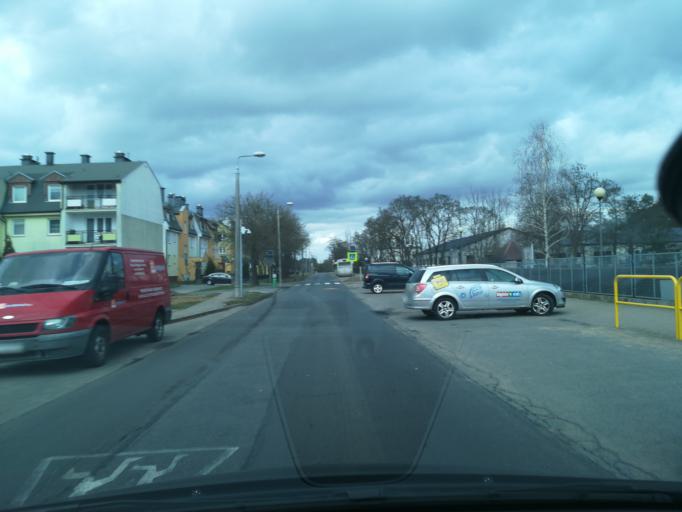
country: PL
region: Kujawsko-Pomorskie
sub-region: Powiat torunski
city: Lubicz Dolny
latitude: 52.9807
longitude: 18.6852
